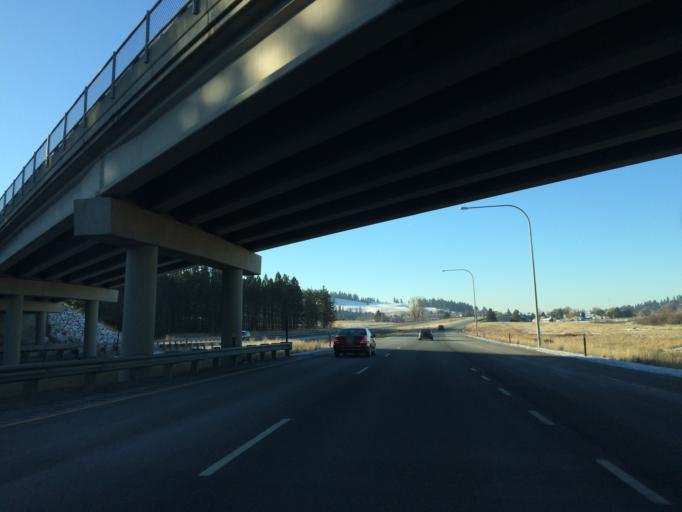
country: US
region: Washington
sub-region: Spokane County
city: Fairchild Air Force Base
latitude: 47.5660
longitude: -117.5934
